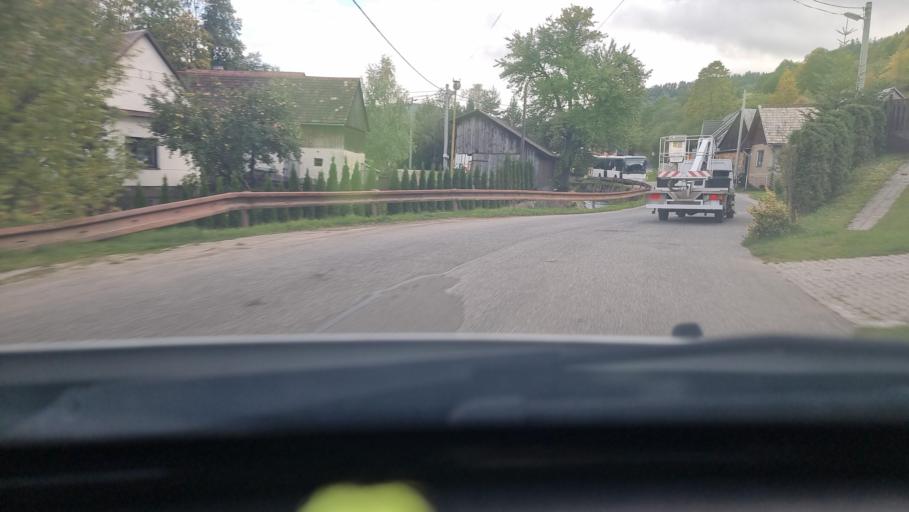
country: PL
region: Lesser Poland Voivodeship
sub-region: Powiat nowotarski
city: Szczawnica
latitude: 49.3294
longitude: 20.4373
